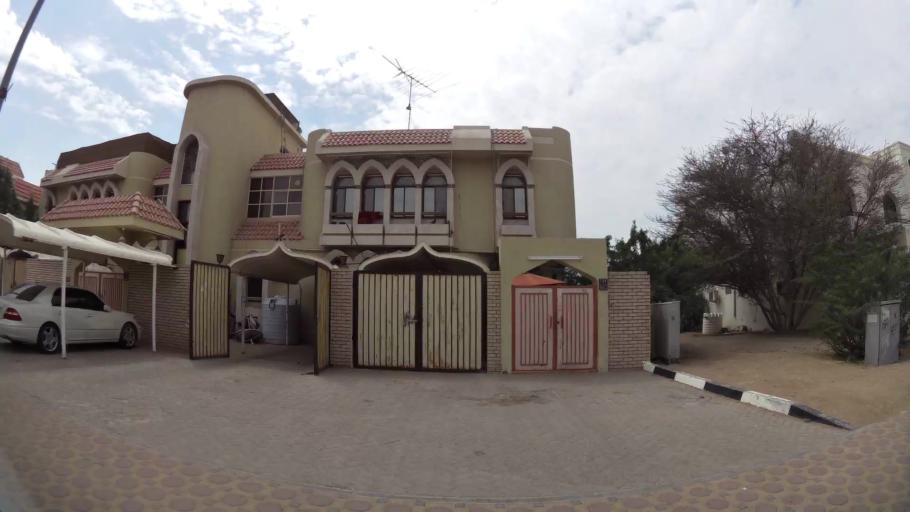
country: OM
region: Al Buraimi
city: Al Buraymi
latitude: 24.2244
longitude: 55.7870
